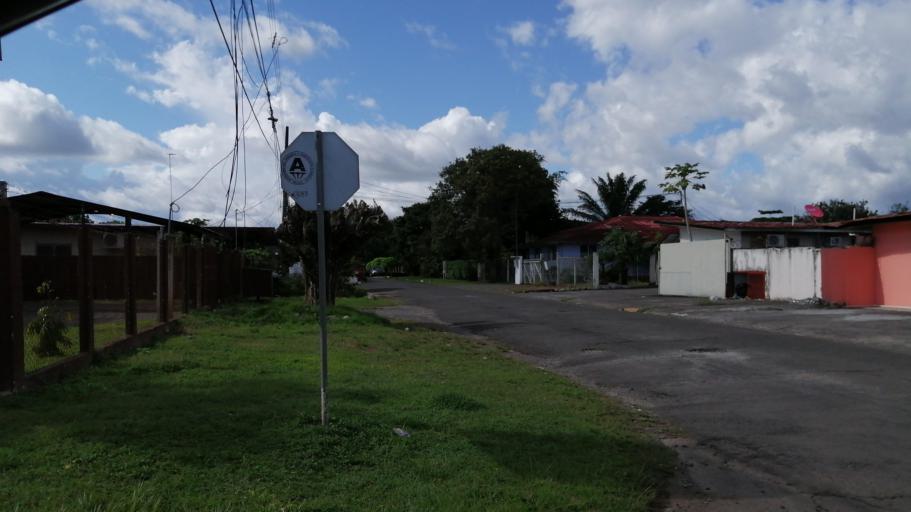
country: PA
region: Chiriqui
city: David
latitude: 8.4341
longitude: -82.4338
